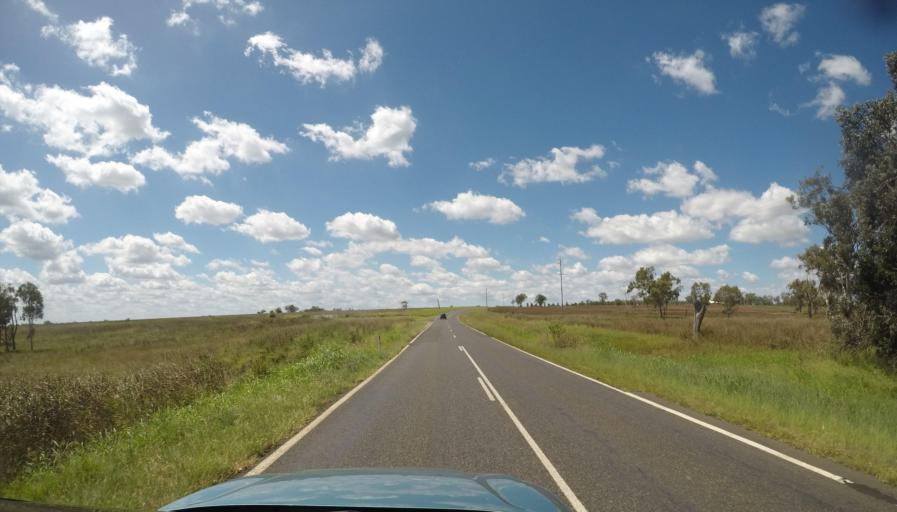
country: AU
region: Queensland
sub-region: Toowoomba
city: Oakey
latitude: -27.5548
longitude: 151.7066
